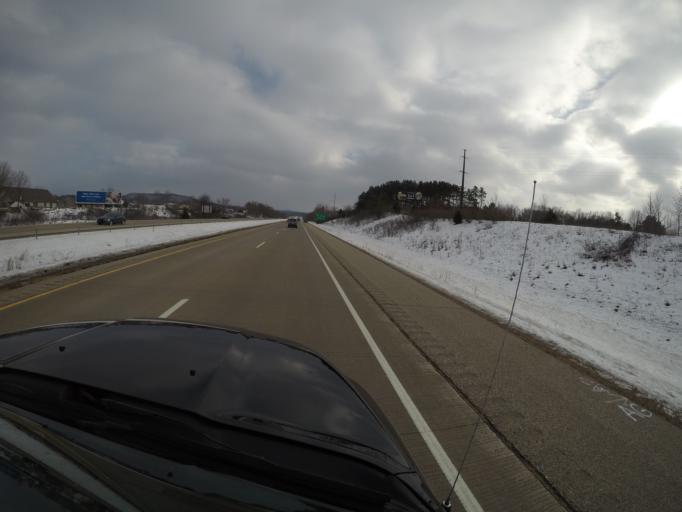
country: US
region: Wisconsin
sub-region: La Crosse County
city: Holmen
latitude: 43.9531
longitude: -91.2769
